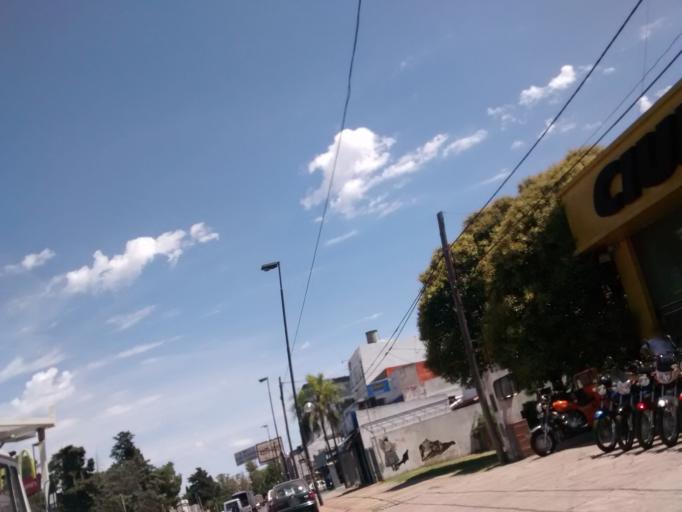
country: AR
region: Buenos Aires
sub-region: Partido de La Plata
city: La Plata
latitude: -34.8831
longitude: -58.0060
